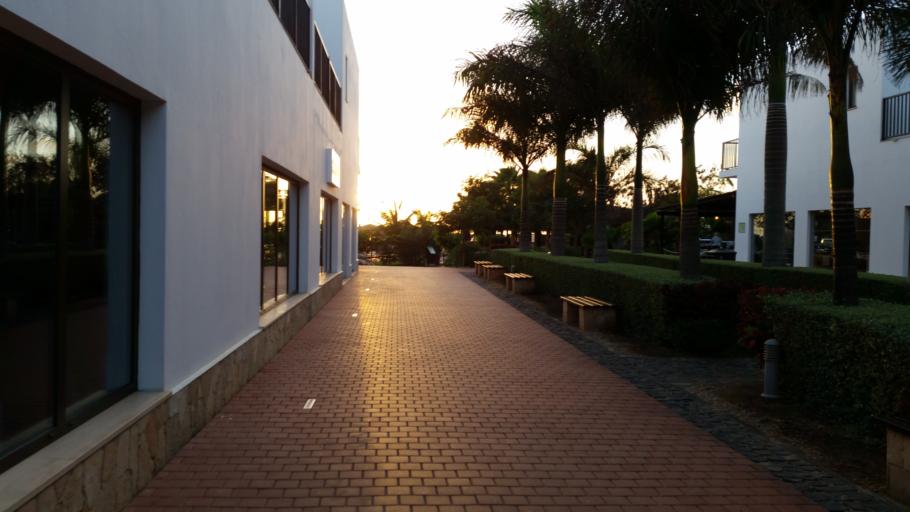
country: CV
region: Sal
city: Santa Maria
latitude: 16.6162
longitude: -22.9268
